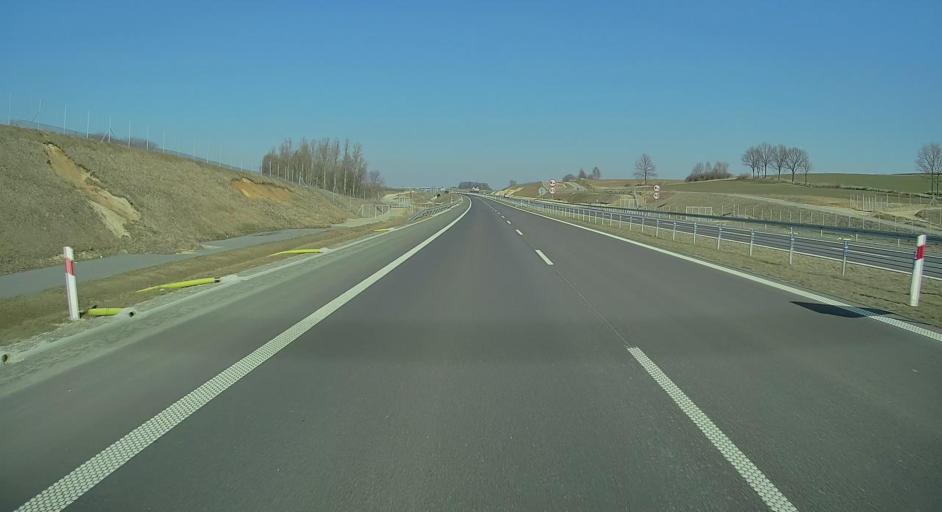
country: PL
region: Lublin Voivodeship
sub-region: Powiat krasnicki
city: Szastarka
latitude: 50.8135
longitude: 22.3000
